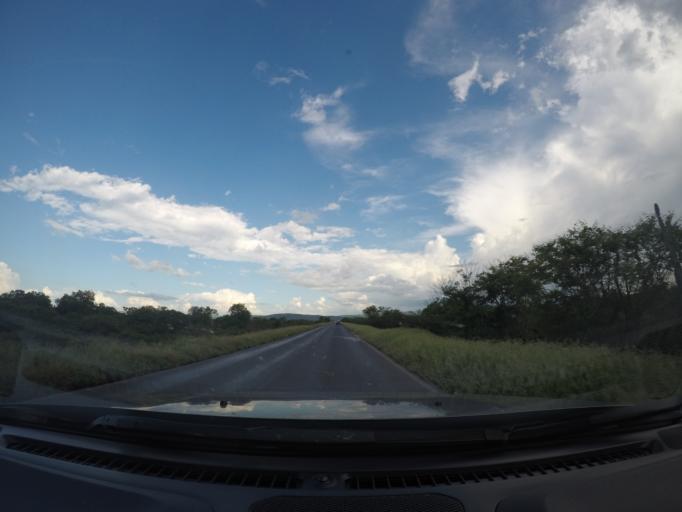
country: BR
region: Bahia
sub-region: Ibotirama
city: Ibotirama
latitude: -12.1756
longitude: -43.2516
